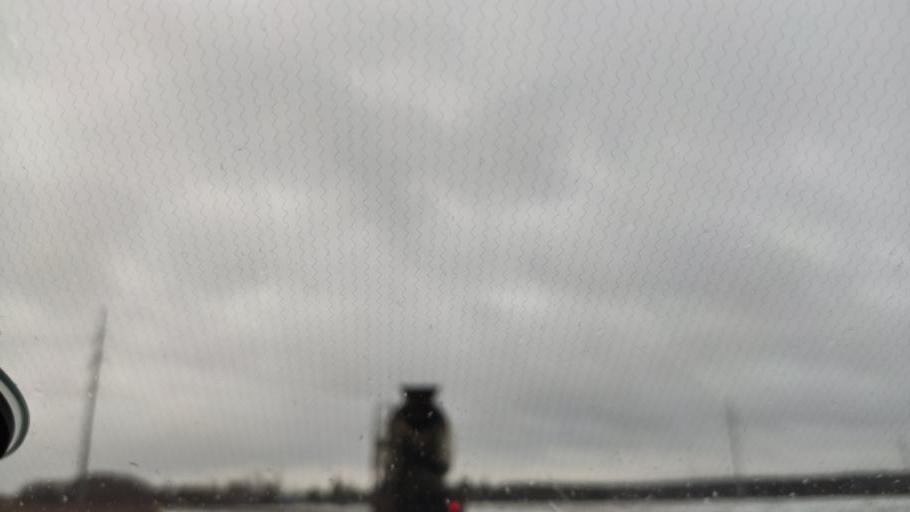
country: RU
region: Moskovskaya
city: Vatutinki
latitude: 55.4681
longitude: 37.3501
